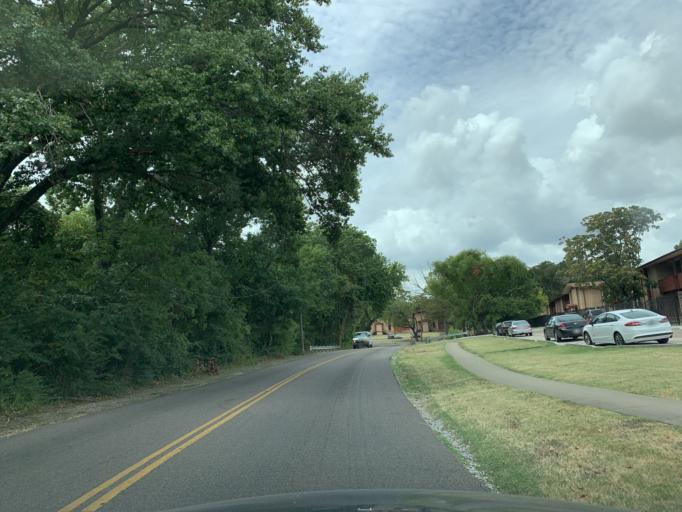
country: US
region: Texas
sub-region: Dallas County
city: Cockrell Hill
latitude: 32.7527
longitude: -96.8599
